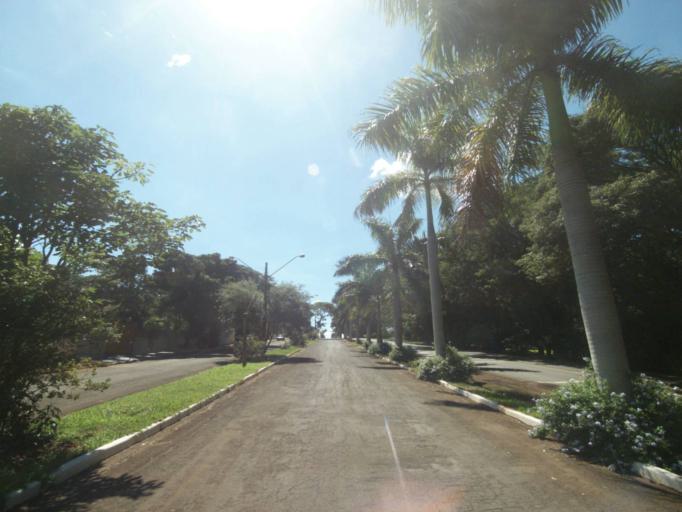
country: BR
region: Parana
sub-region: Sertanopolis
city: Sertanopolis
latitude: -23.0337
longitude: -50.8172
